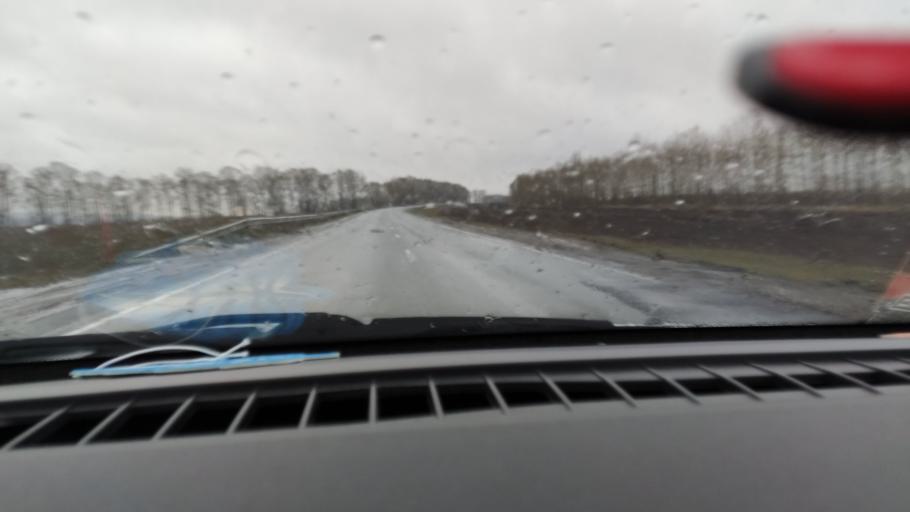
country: RU
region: Tatarstan
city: Mendeleyevsk
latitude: 55.8488
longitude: 52.2091
